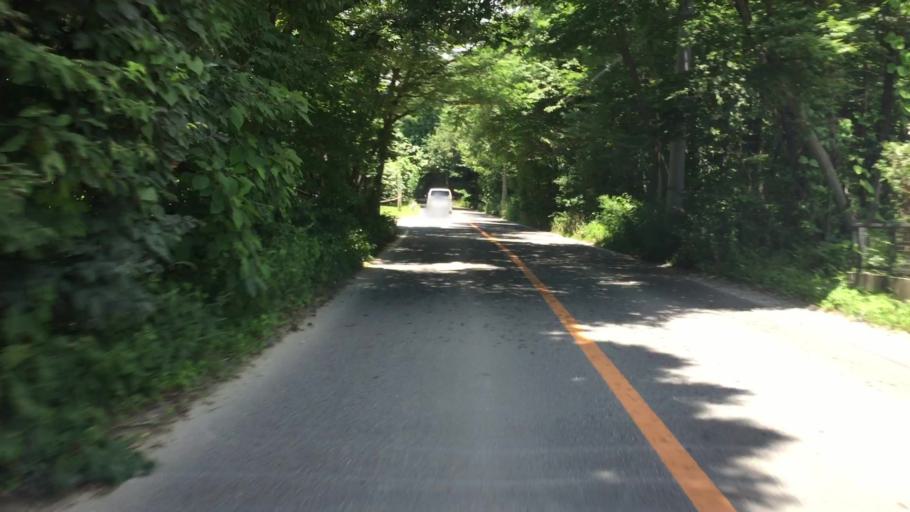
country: JP
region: Tochigi
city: Kuroiso
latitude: 37.0244
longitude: 140.0047
